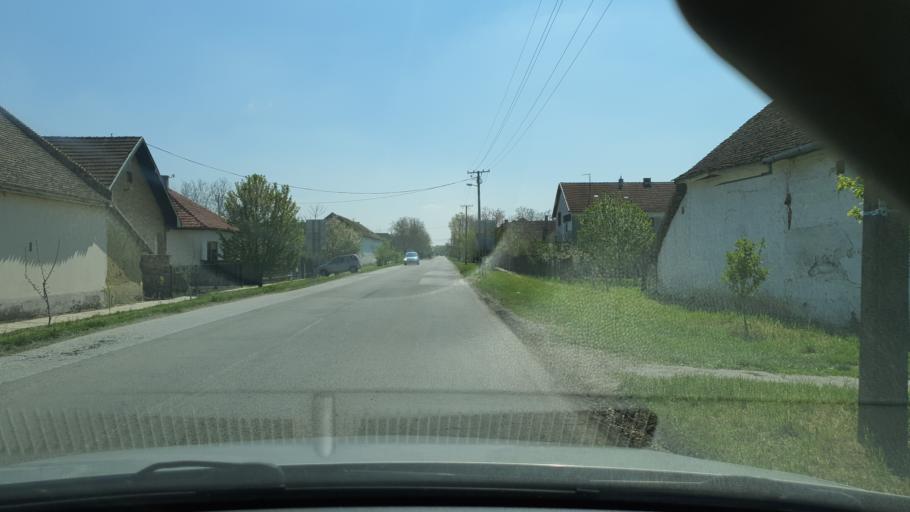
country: RS
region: Autonomna Pokrajina Vojvodina
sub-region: Zapadnobacki Okrug
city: Odzaci
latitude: 45.4583
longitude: 19.3310
